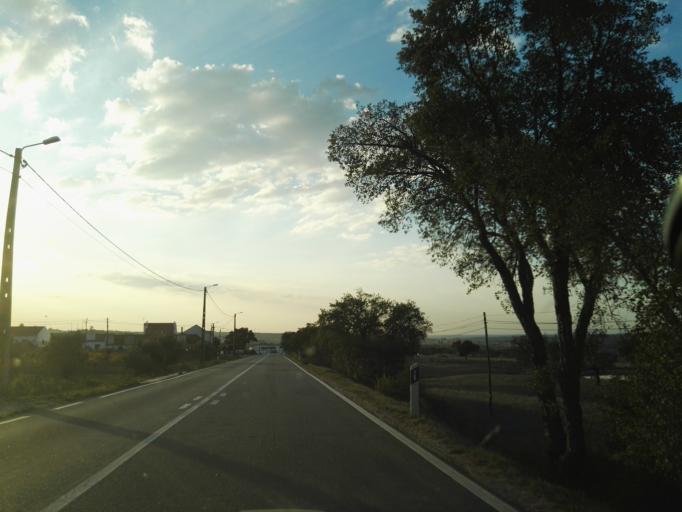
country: PT
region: Evora
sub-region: Mora
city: Mora
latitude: 38.9436
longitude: -8.1371
